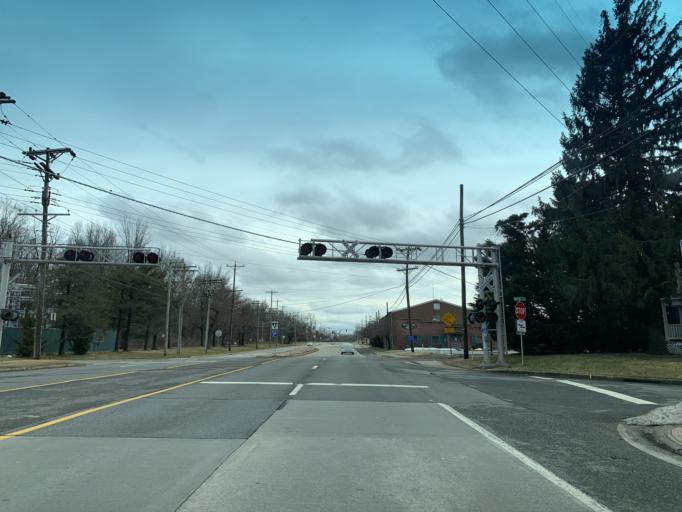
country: US
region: Delaware
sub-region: New Castle County
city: New Castle
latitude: 39.6724
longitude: -75.5612
